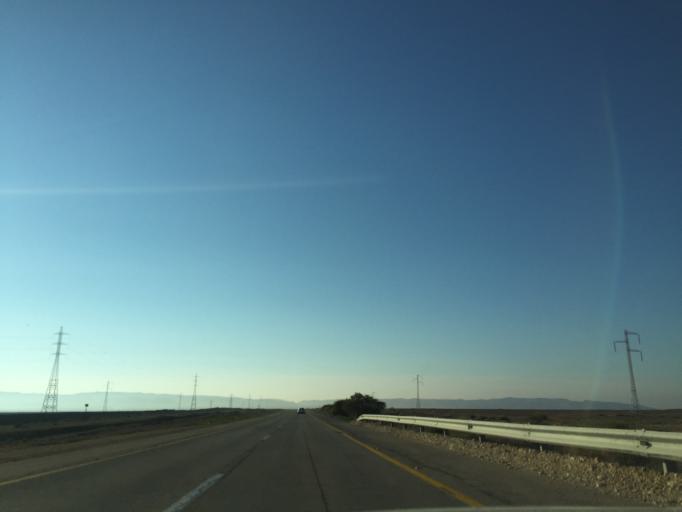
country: IL
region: Southern District
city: Mitzpe Ramon
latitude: 30.4366
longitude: 34.9397
